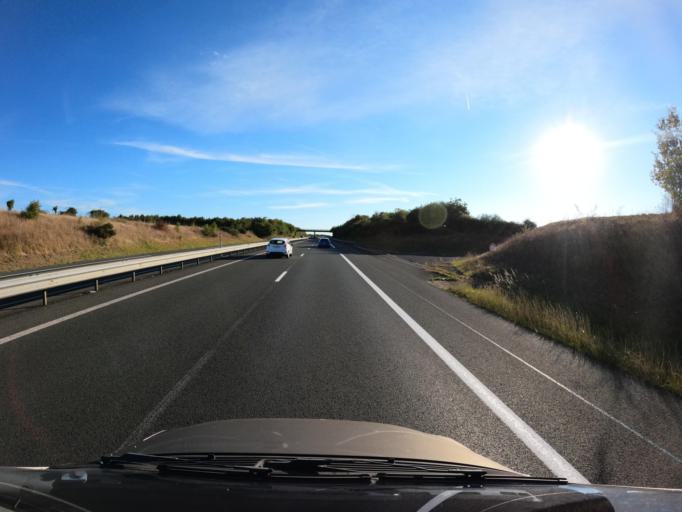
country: FR
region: Pays de la Loire
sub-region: Departement de Maine-et-Loire
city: Chemille-Melay
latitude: 47.2144
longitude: -0.7636
